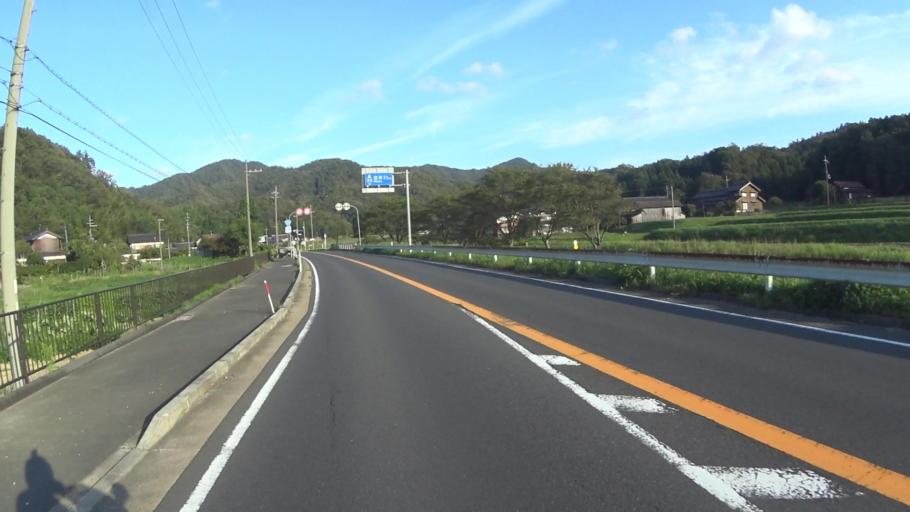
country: JP
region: Hyogo
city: Toyooka
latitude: 35.5736
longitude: 134.9787
